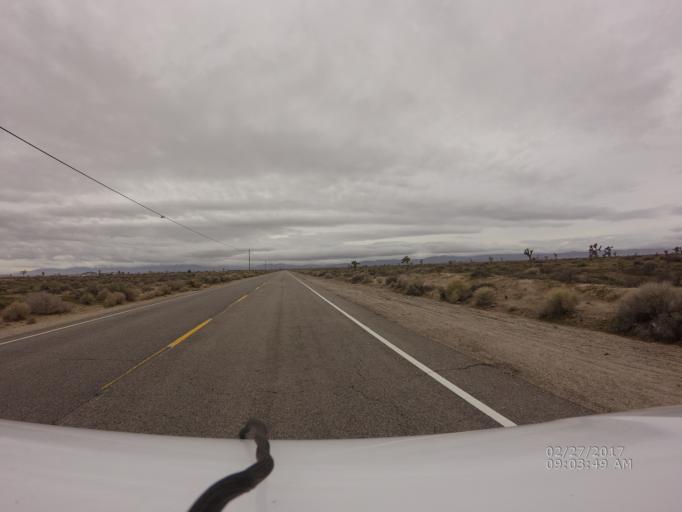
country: US
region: California
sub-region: Los Angeles County
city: Lancaster
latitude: 34.7424
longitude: -118.0770
